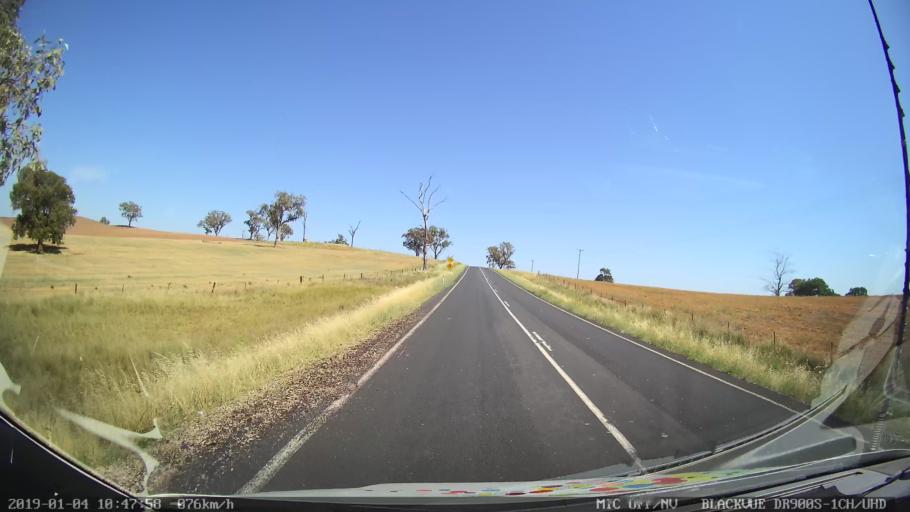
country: AU
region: New South Wales
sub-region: Cabonne
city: Molong
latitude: -33.2648
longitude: 148.7161
